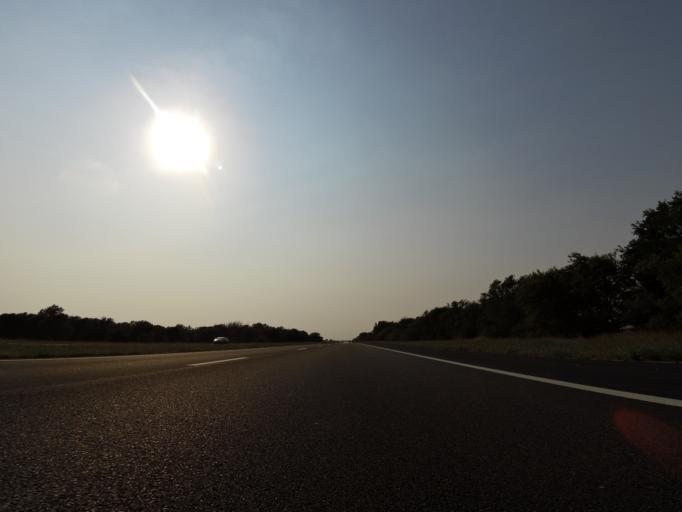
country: US
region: Kansas
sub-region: Reno County
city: Haven
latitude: 37.8845
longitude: -97.7292
